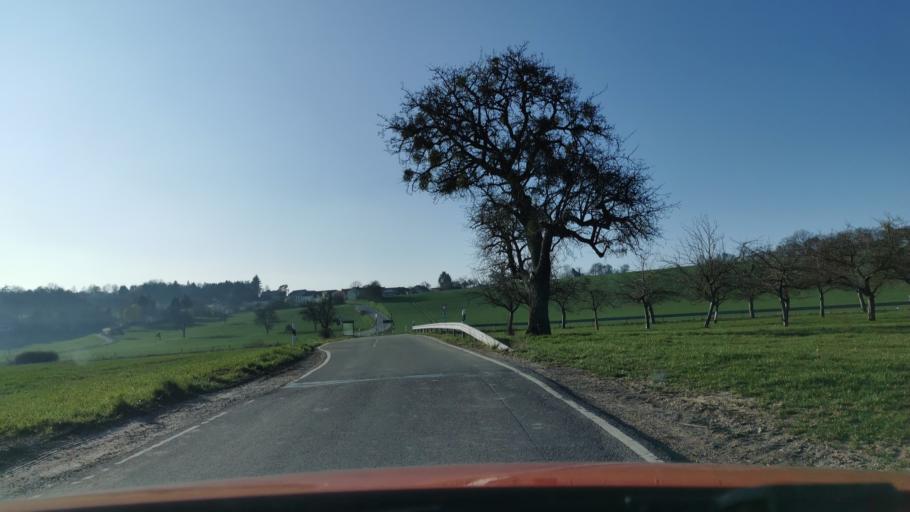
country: DE
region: Rheinland-Pfalz
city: Trierweiler
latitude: 49.7906
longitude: 6.5508
